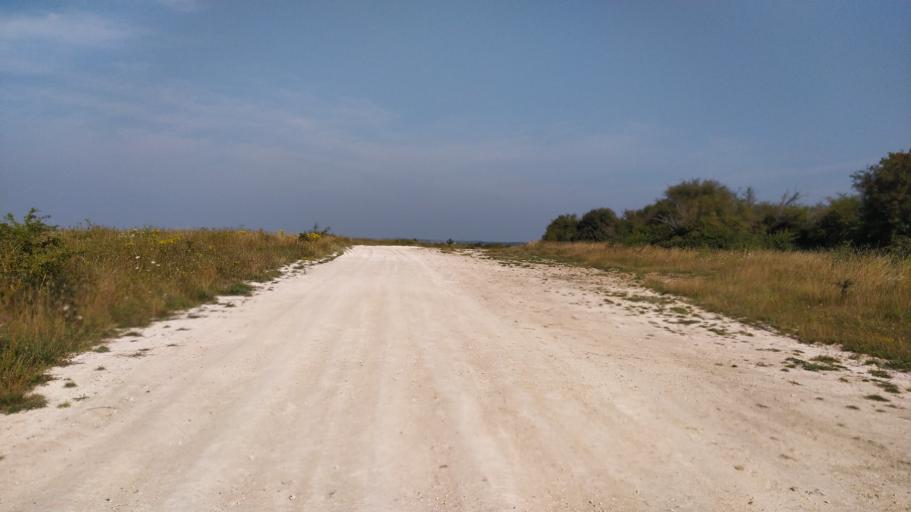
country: GB
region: England
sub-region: Wiltshire
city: Shrewton
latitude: 51.1849
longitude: -1.9513
